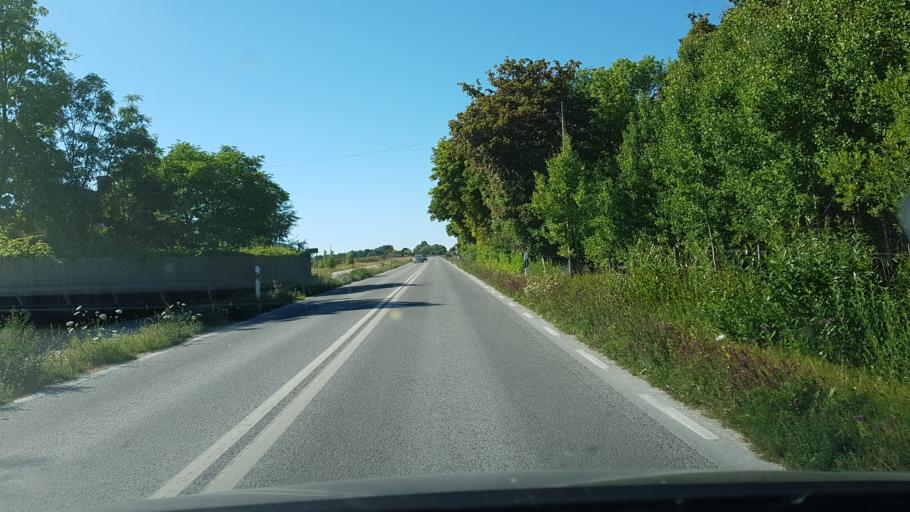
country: SE
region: Gotland
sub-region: Gotland
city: Klintehamn
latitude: 57.4470
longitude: 18.1424
